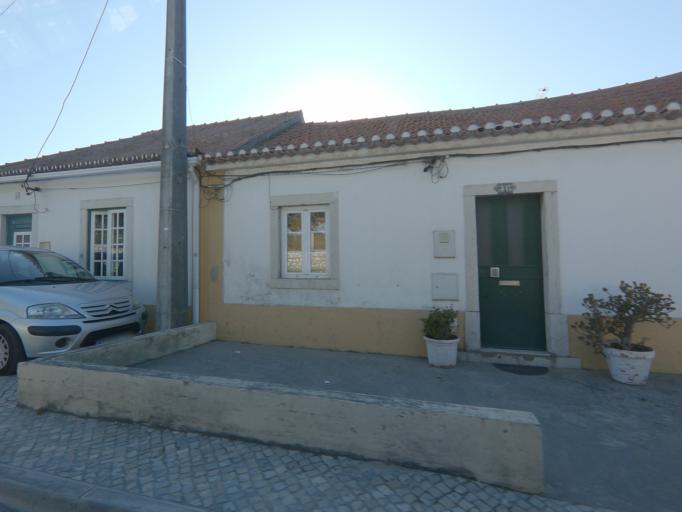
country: PT
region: Setubal
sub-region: Palmela
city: Quinta do Anjo
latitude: 38.5327
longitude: -8.9890
